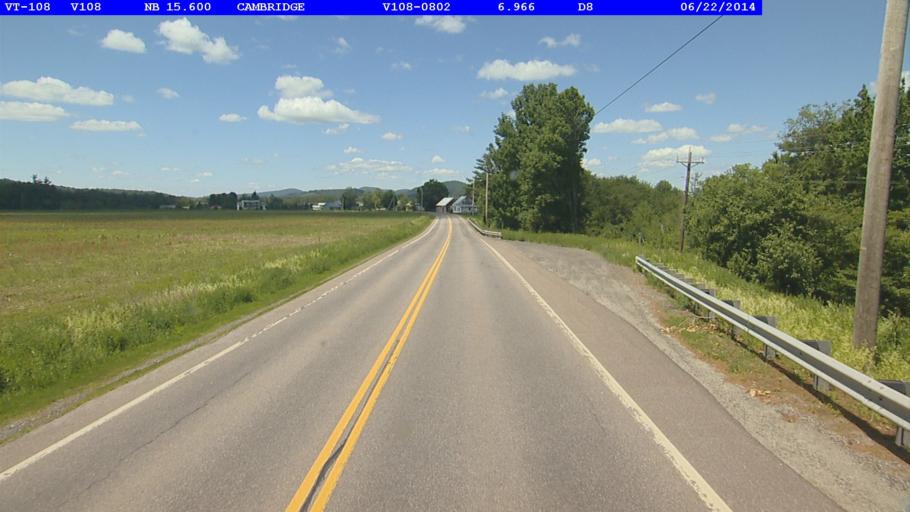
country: US
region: Vermont
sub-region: Lamoille County
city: Johnson
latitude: 44.6214
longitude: -72.8241
